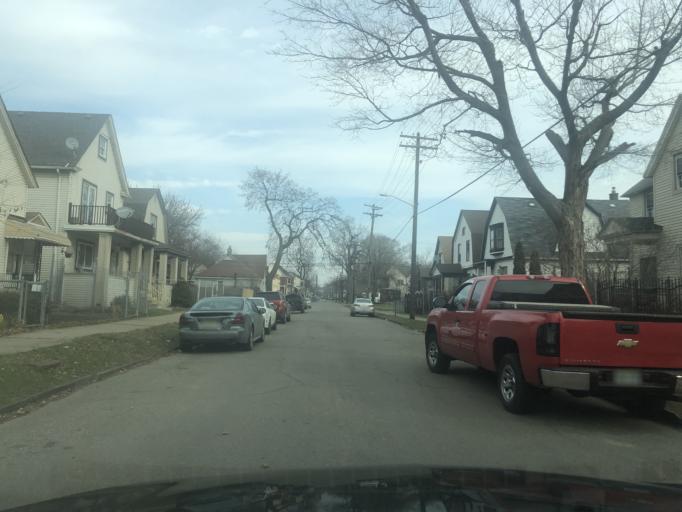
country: US
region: Michigan
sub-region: Wayne County
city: River Rouge
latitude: 42.3150
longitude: -83.1013
